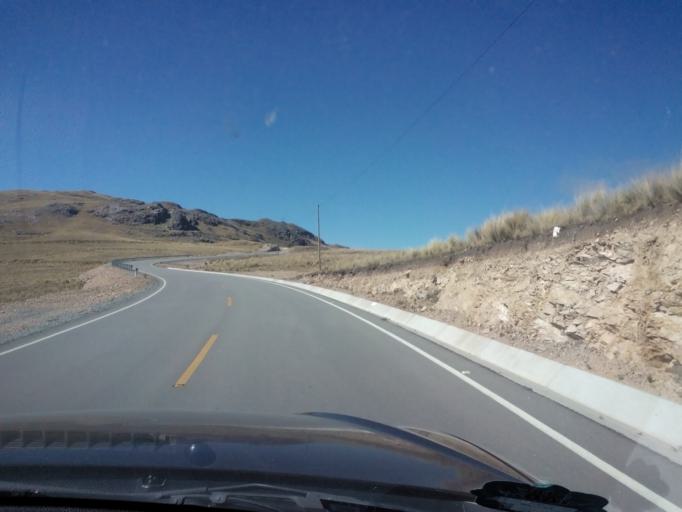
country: PE
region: Ayacucho
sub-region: Provincia de Huamanga
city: Chiara
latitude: -13.3610
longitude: -74.0853
